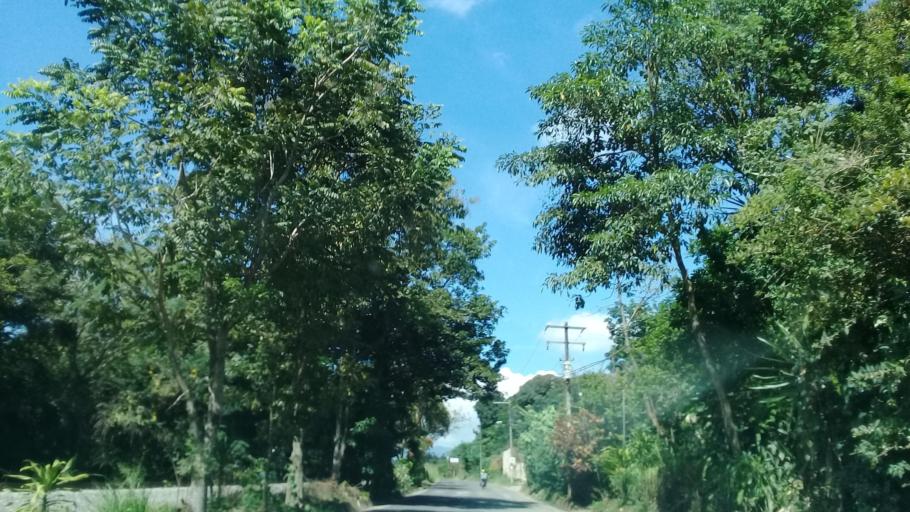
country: MX
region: Veracruz
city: Amatlan de los Reyes
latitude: 18.8387
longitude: -96.9211
